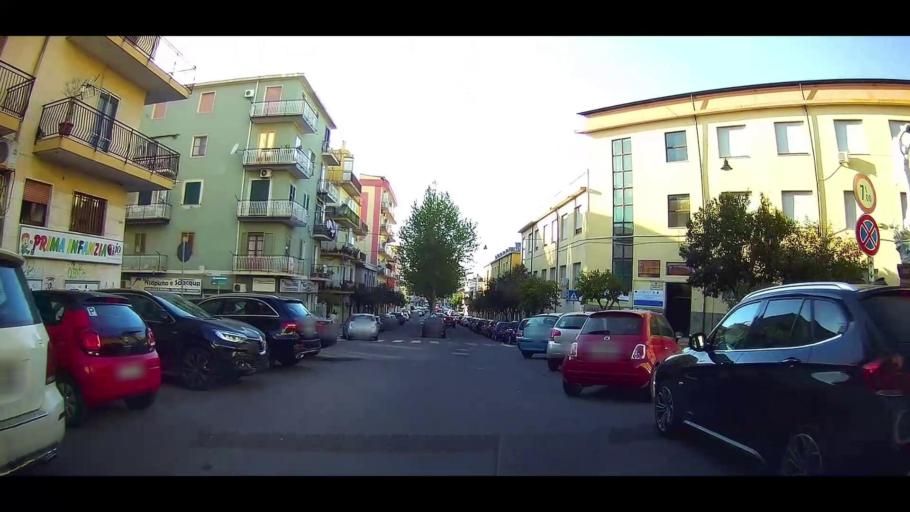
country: IT
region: Calabria
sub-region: Provincia di Crotone
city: Crotone
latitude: 39.0771
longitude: 17.1281
